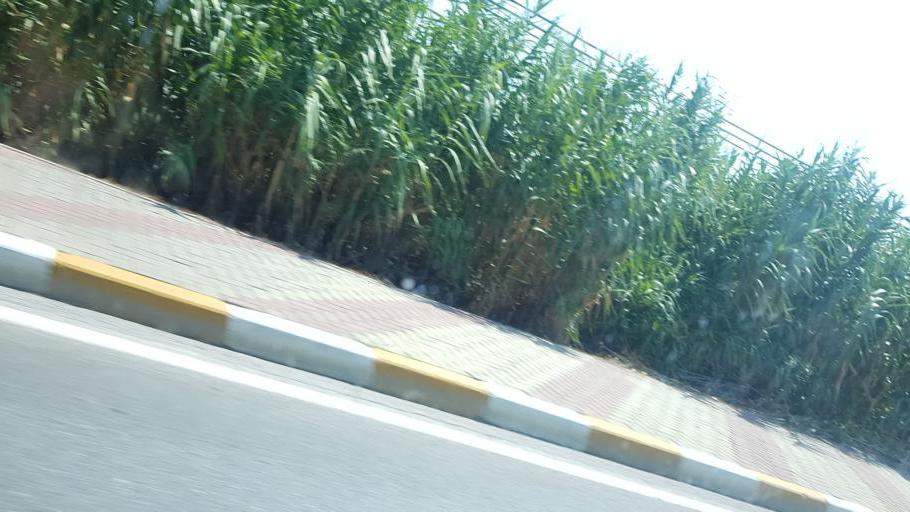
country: TR
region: Izmir
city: Urla
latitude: 38.3471
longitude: 26.7718
